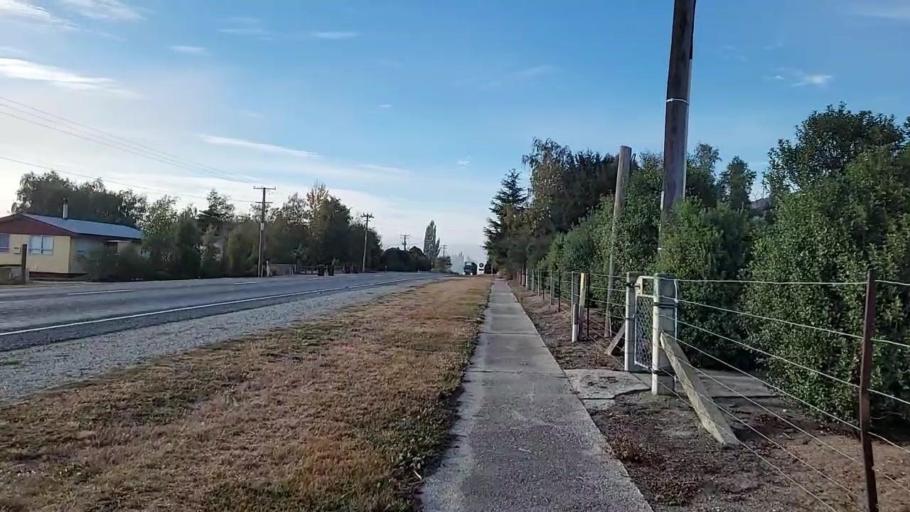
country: NZ
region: Southland
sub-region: Gore District
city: Gore
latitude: -45.6396
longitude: 169.3709
